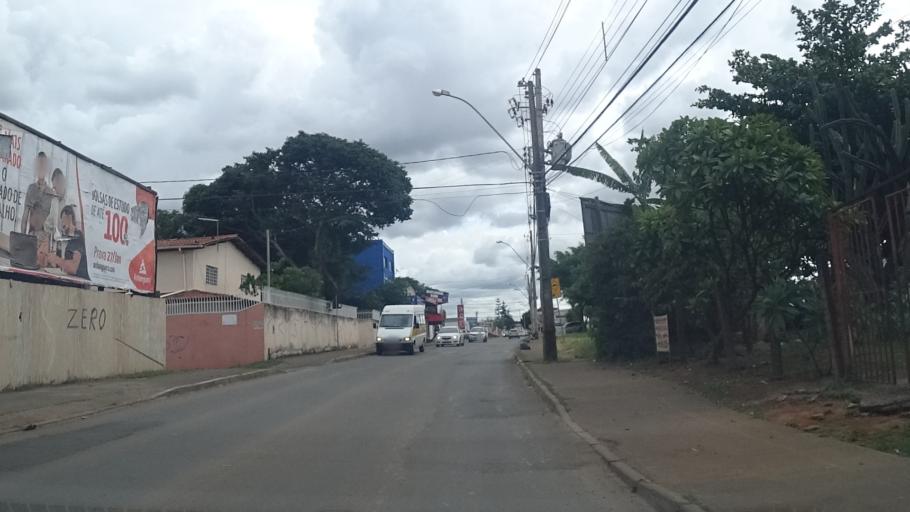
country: BR
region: Federal District
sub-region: Brasilia
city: Brasilia
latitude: -15.8517
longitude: -48.0292
